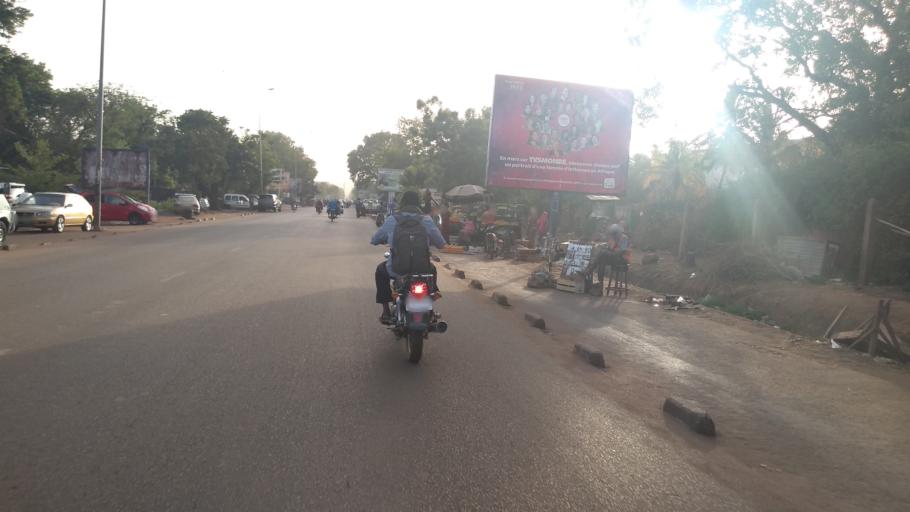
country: ML
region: Bamako
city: Bamako
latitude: 12.6431
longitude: -8.0178
